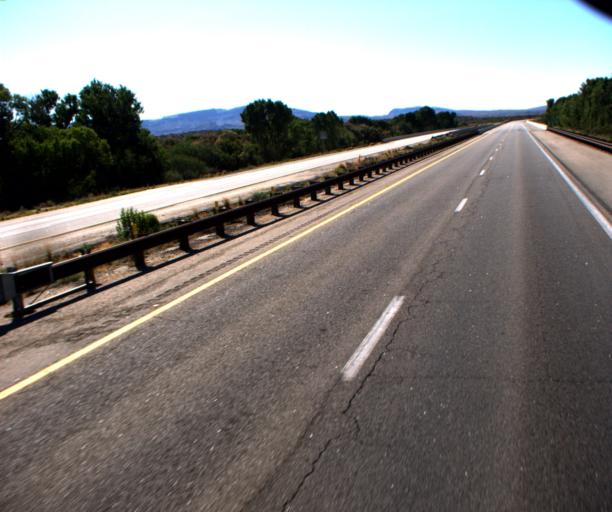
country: US
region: Arizona
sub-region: Yavapai County
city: Bagdad
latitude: 34.6653
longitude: -113.5839
